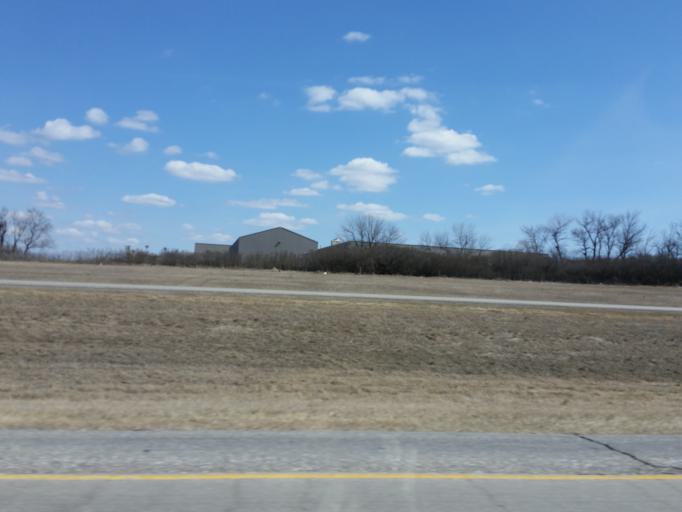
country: US
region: South Dakota
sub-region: Codington County
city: Watertown
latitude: 44.8968
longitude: -97.0569
